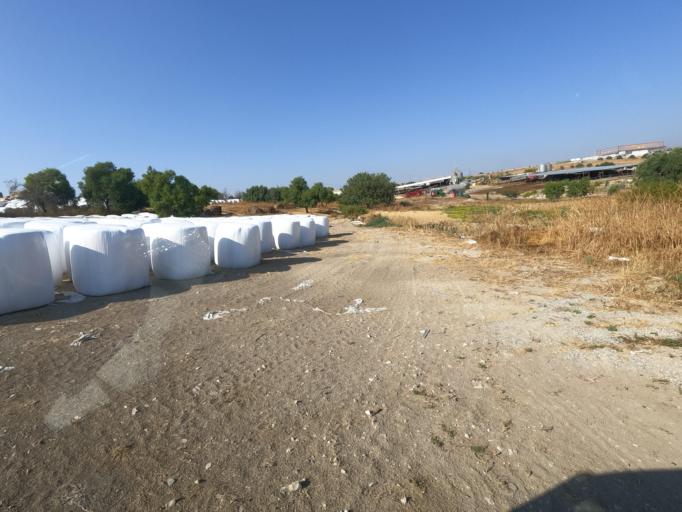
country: CY
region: Lefkosia
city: Lympia
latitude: 34.9888
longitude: 33.4695
